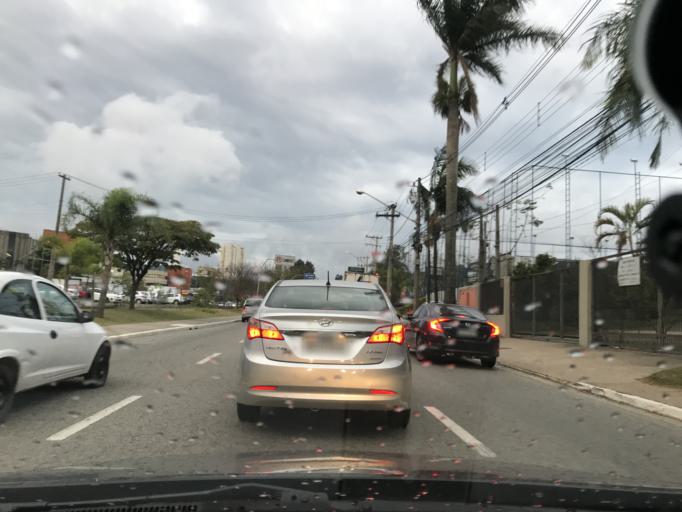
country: BR
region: Sao Paulo
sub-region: Carapicuiba
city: Carapicuiba
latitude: -23.5021
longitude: -46.8318
